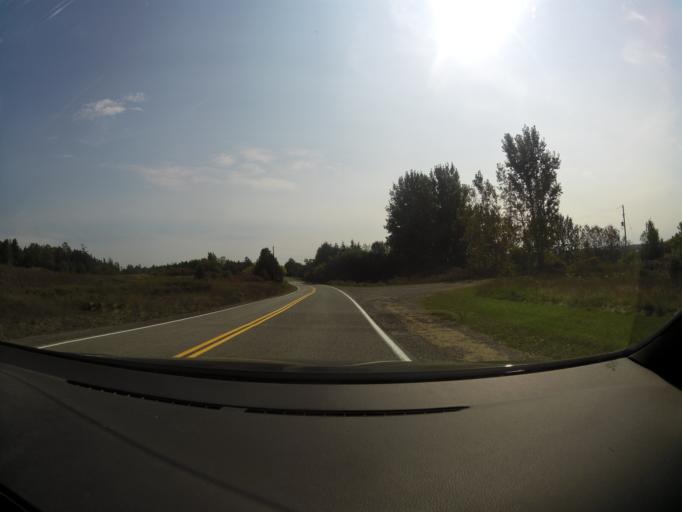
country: CA
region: Ontario
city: Arnprior
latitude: 45.3394
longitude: -76.1922
